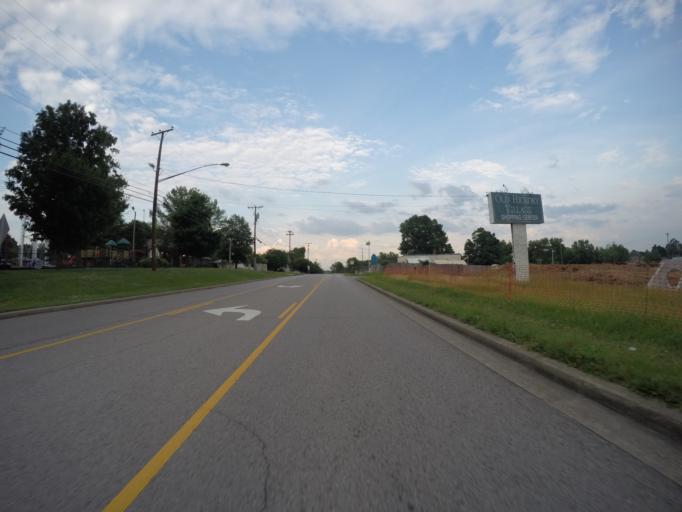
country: US
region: Tennessee
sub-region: Davidson County
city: Lakewood
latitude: 36.2641
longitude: -86.6489
